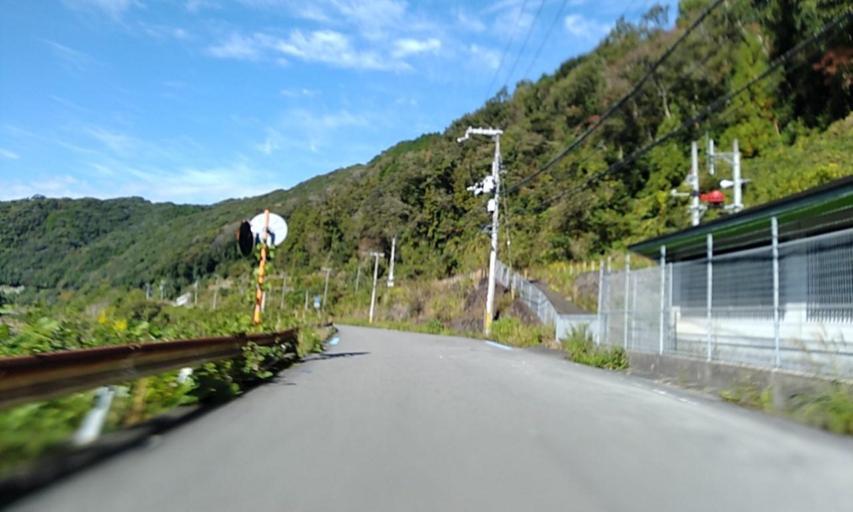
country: JP
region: Wakayama
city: Kainan
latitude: 34.0558
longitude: 135.3391
